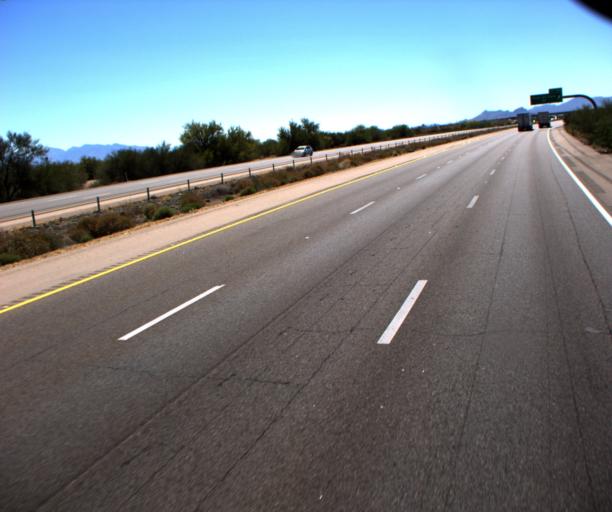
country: US
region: Arizona
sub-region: Pima County
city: Avra Valley
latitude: 32.5116
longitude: -111.2718
